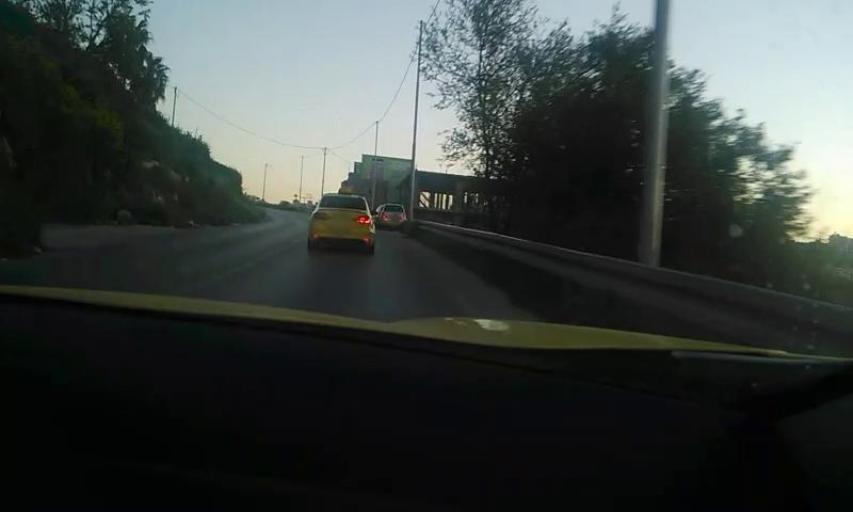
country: PS
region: West Bank
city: Jifna
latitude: 31.9520
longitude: 35.2152
